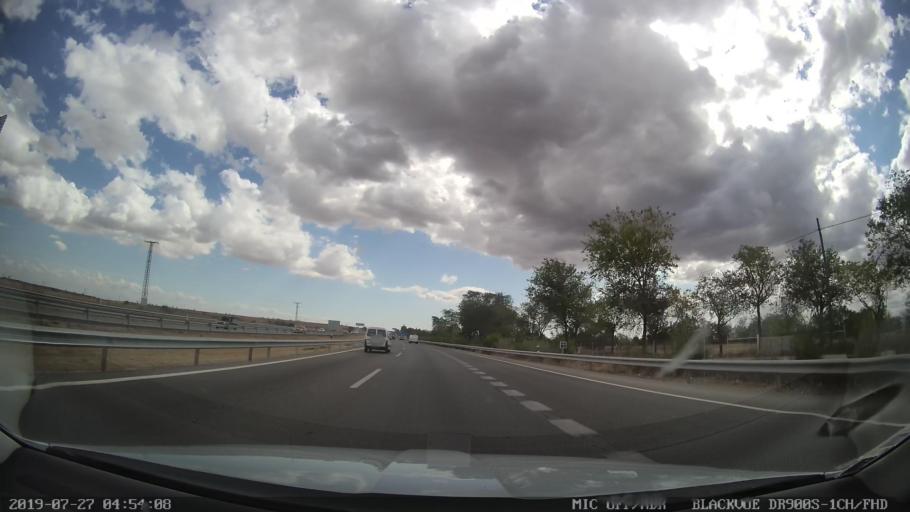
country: ES
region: Madrid
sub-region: Provincia de Madrid
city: Navalcarnero
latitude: 40.2765
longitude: -4.0294
